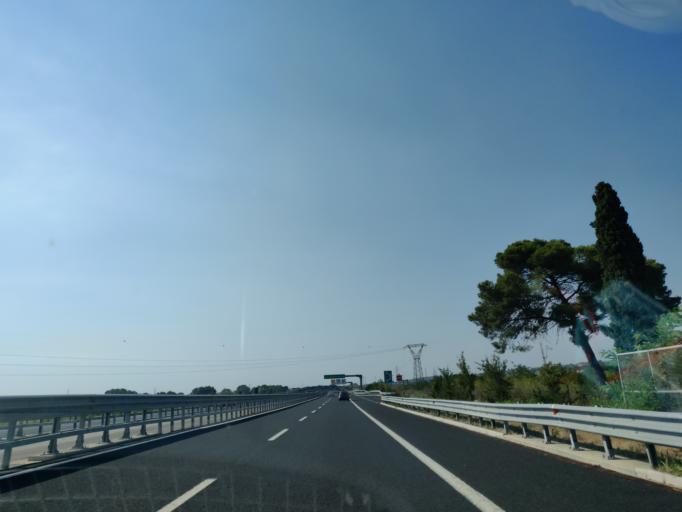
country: IT
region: Latium
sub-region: Provincia di Viterbo
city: Tarquinia
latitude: 42.2487
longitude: 11.7361
